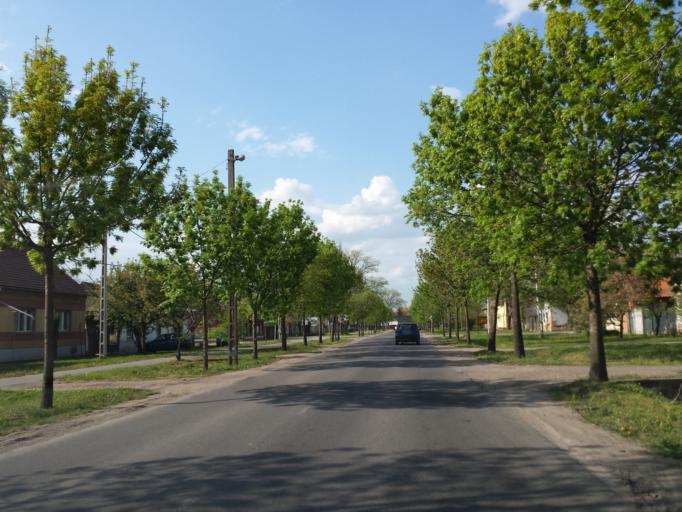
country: HU
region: Csongrad
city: Mako
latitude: 46.2329
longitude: 20.4803
